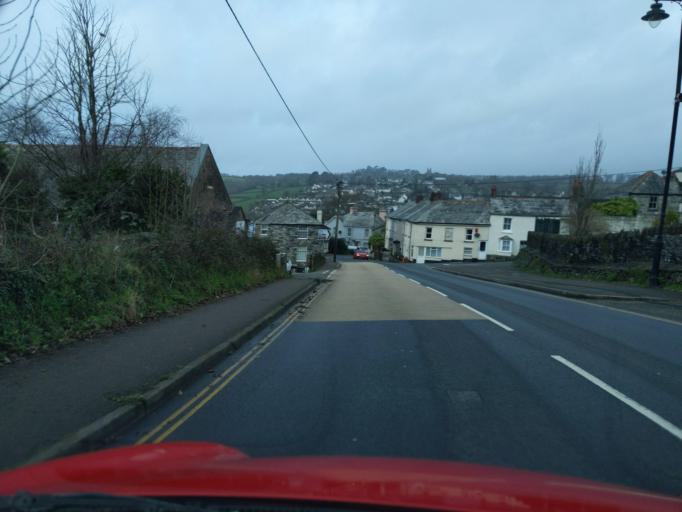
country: GB
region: England
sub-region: Cornwall
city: Launceston
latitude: 50.6383
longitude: -4.3633
